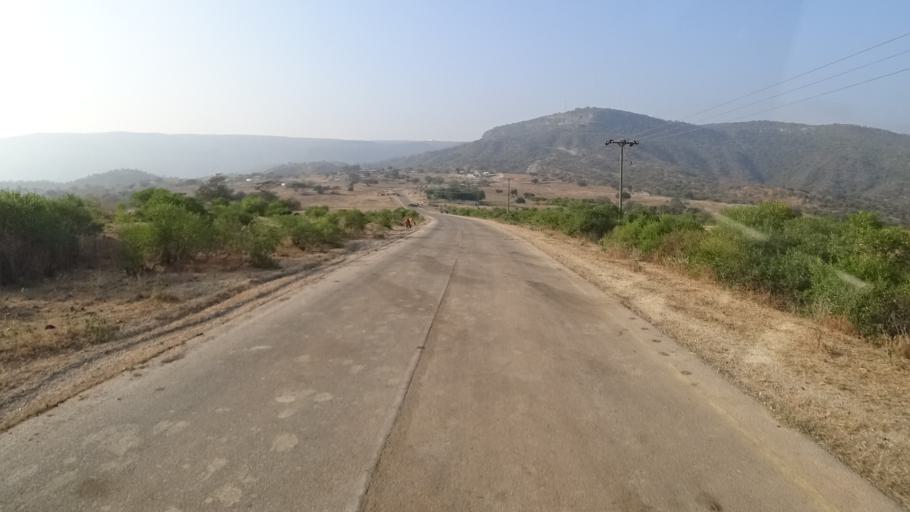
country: YE
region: Al Mahrah
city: Hawf
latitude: 16.7495
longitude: 53.3432
